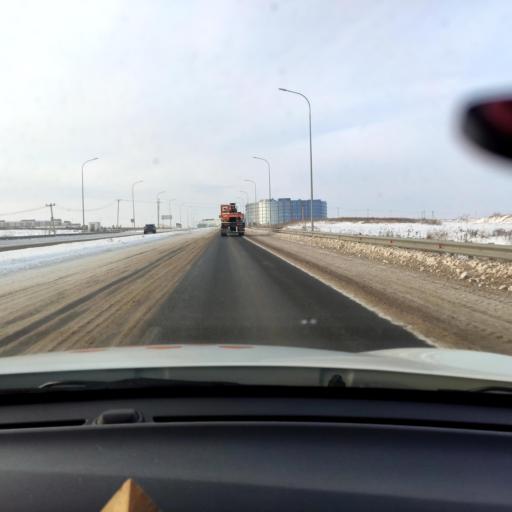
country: RU
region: Tatarstan
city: Sviyazhsk
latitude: 55.7484
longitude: 48.7611
